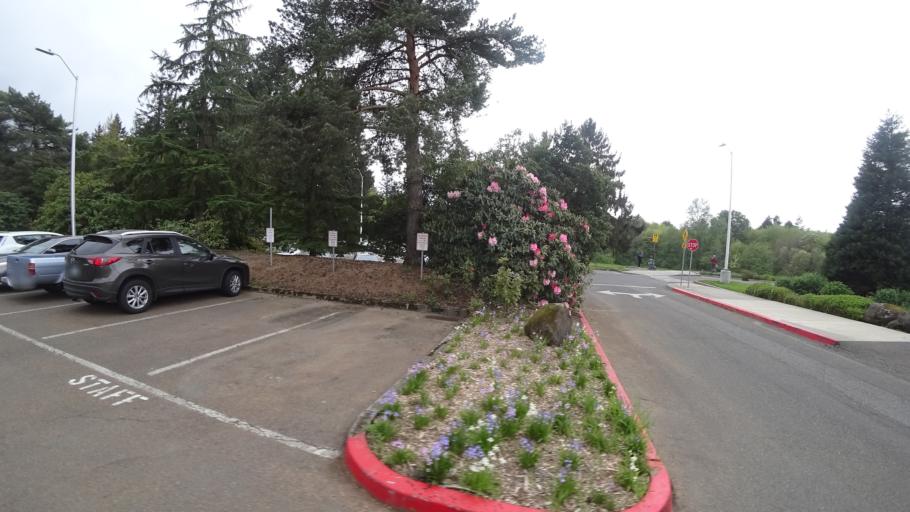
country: US
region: Oregon
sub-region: Washington County
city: Metzger
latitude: 45.4381
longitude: -122.7332
